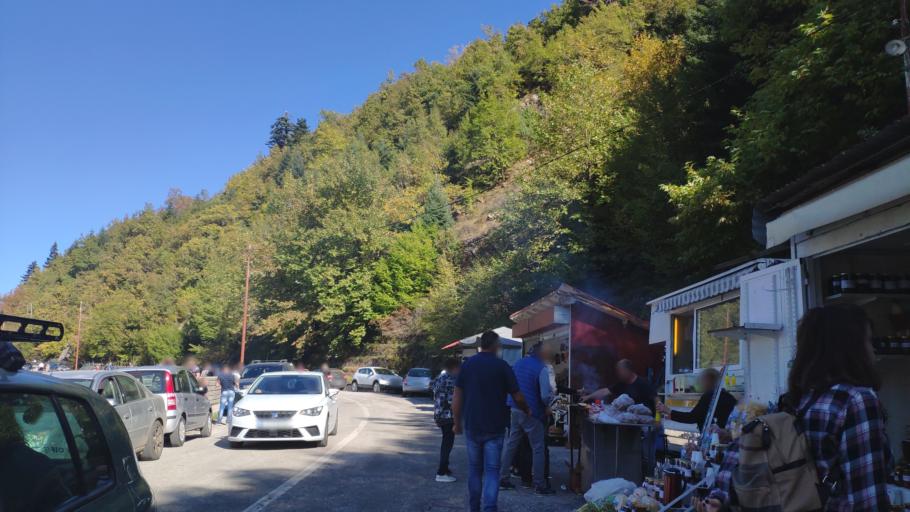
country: GR
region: Thessaly
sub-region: Nomos Kardhitsas
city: Neochori
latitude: 39.2356
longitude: 21.7476
